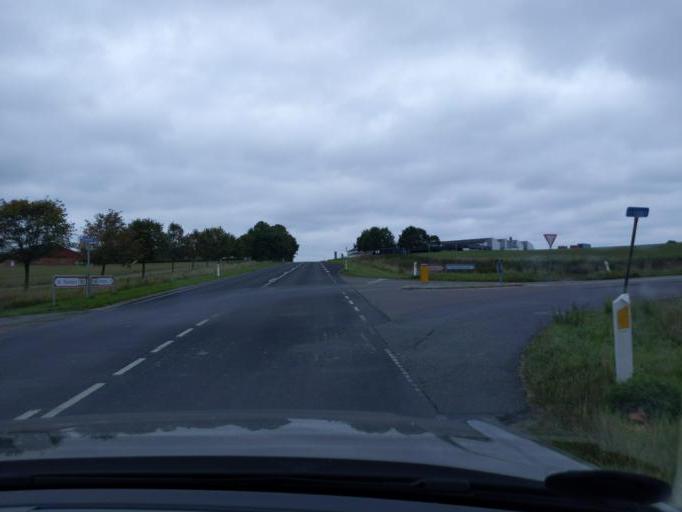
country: DK
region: Central Jutland
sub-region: Randers Kommune
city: Spentrup
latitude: 56.5215
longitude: 9.9356
